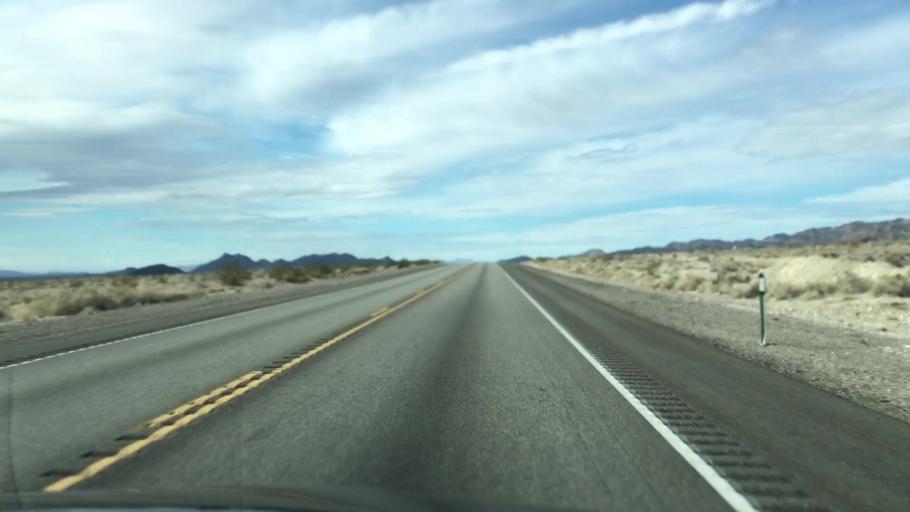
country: US
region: Nevada
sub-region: Nye County
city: Pahrump
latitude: 36.5858
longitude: -116.2142
